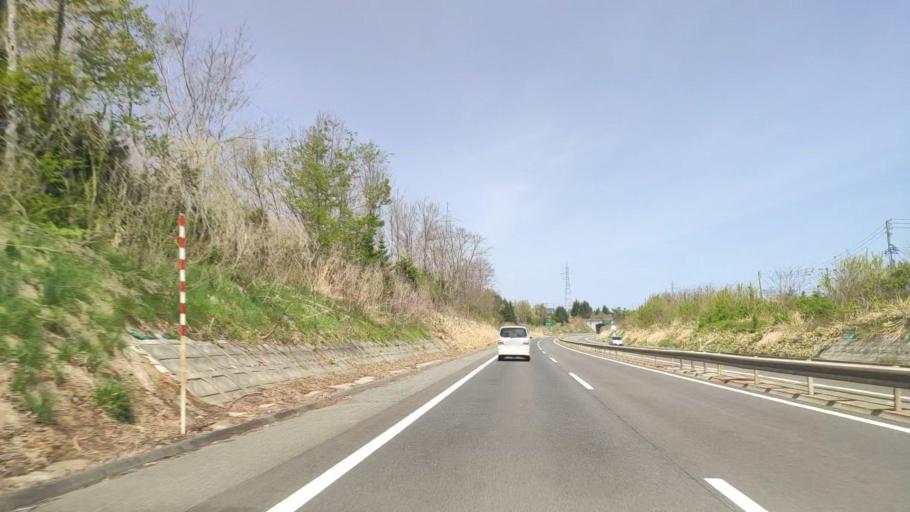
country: JP
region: Aomori
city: Hachinohe
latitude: 40.4743
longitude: 141.4605
